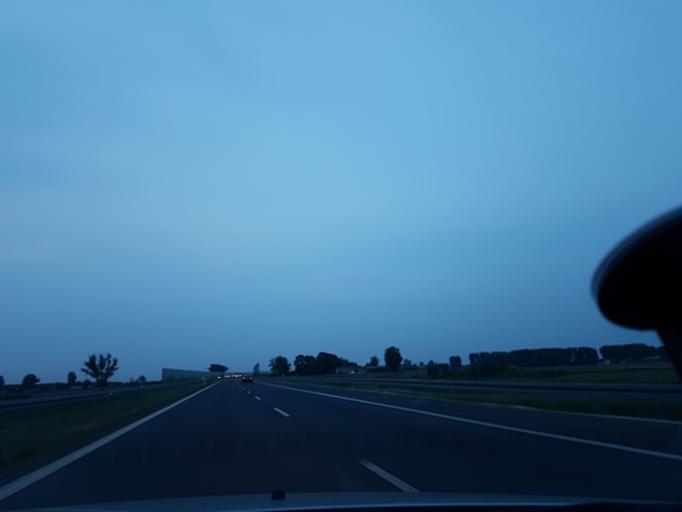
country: PL
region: Lodz Voivodeship
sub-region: Powiat leczycki
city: Piatek
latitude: 52.1226
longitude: 19.4983
